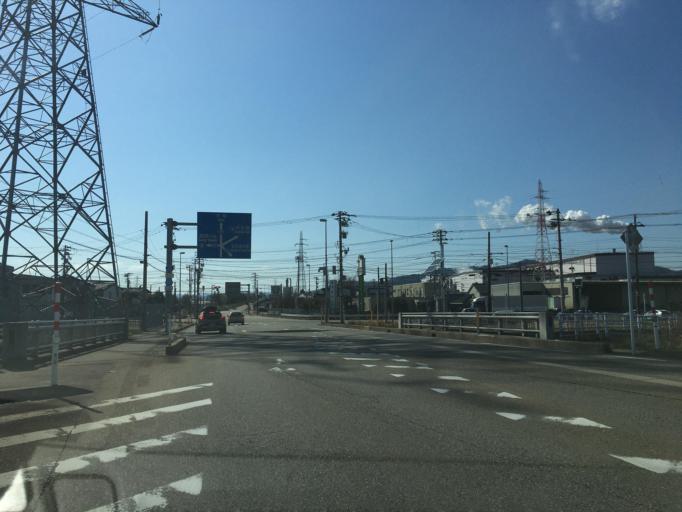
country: JP
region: Toyama
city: Nishishinminato
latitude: 36.7734
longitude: 137.0507
